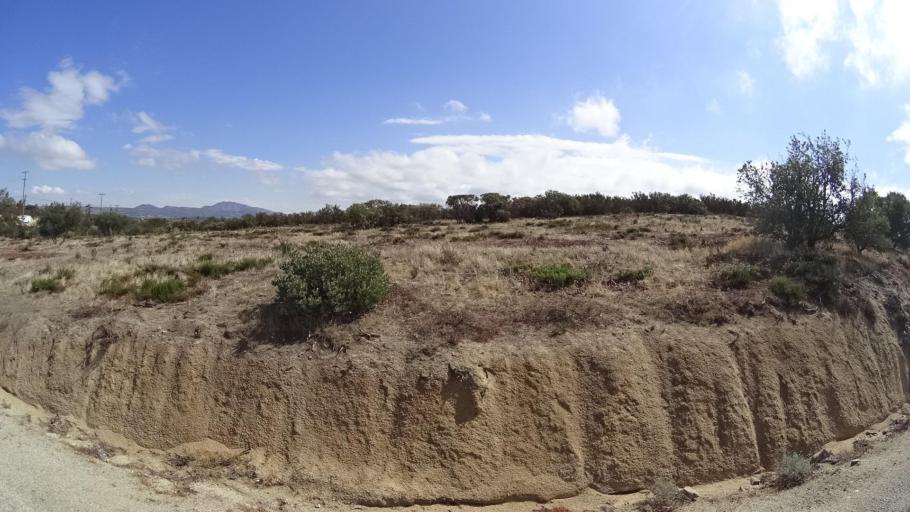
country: US
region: California
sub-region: San Diego County
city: Campo
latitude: 32.6646
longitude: -116.3167
